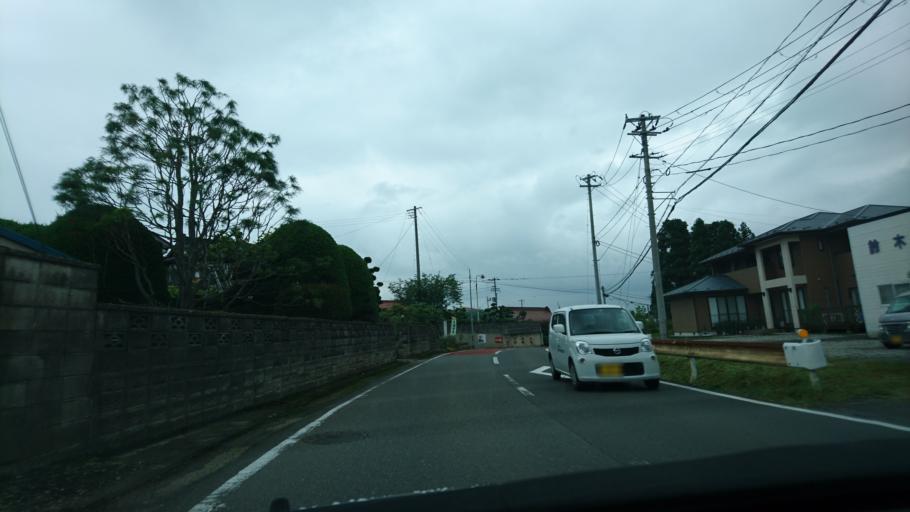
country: JP
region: Iwate
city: Ichinoseki
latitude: 38.8070
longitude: 140.9439
